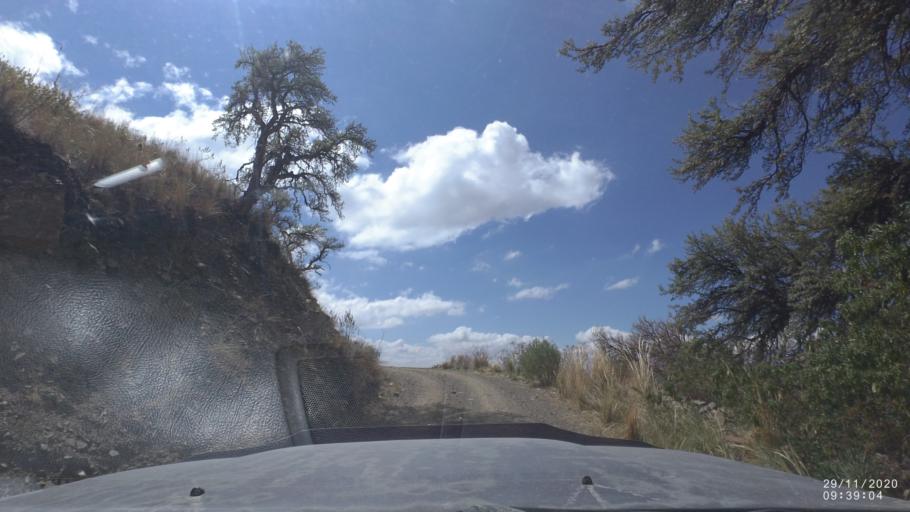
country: BO
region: Cochabamba
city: Cochabamba
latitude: -17.3052
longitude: -66.1845
